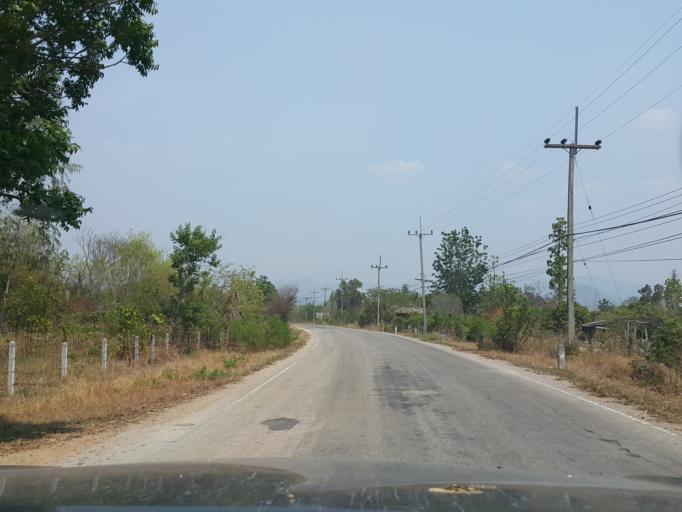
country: TH
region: Lampang
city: Mae Phrik
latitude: 17.5370
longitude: 99.1426
